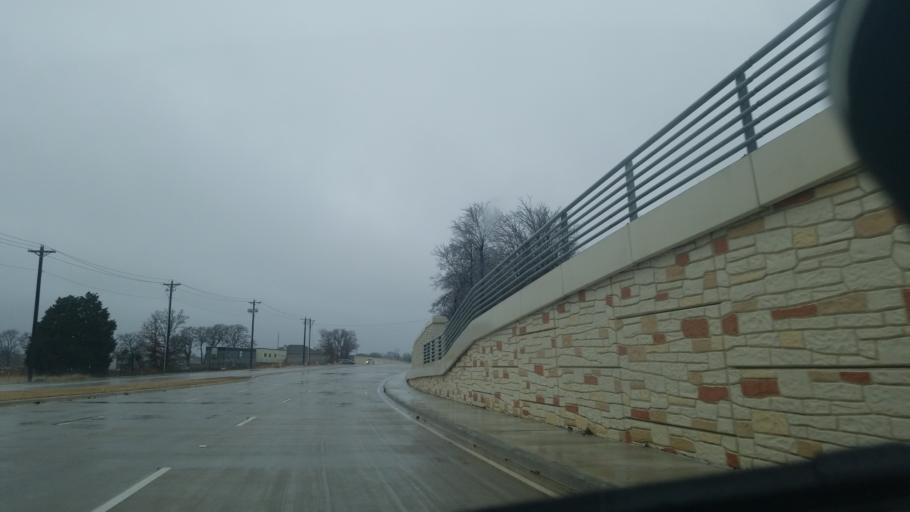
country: US
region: Texas
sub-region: Denton County
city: Corinth
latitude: 33.1448
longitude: -97.0968
